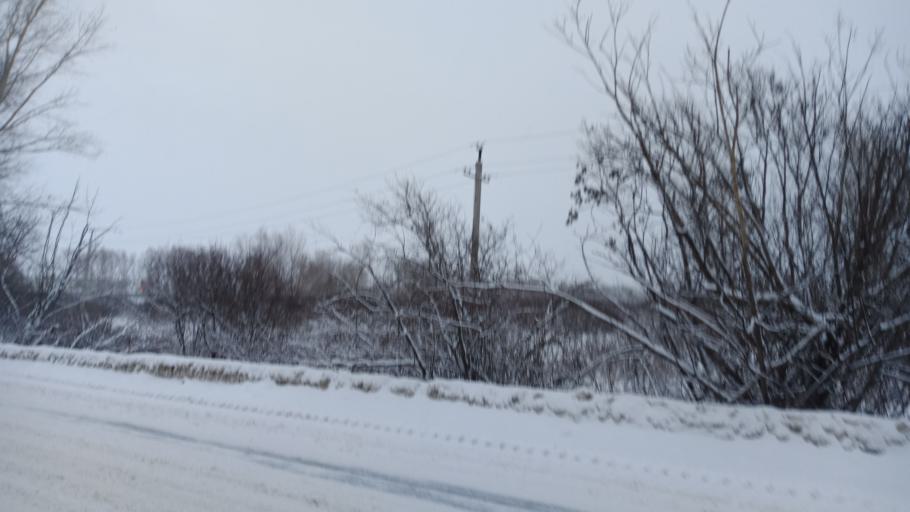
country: RU
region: Altai Krai
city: Zaton
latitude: 53.3125
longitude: 83.8310
